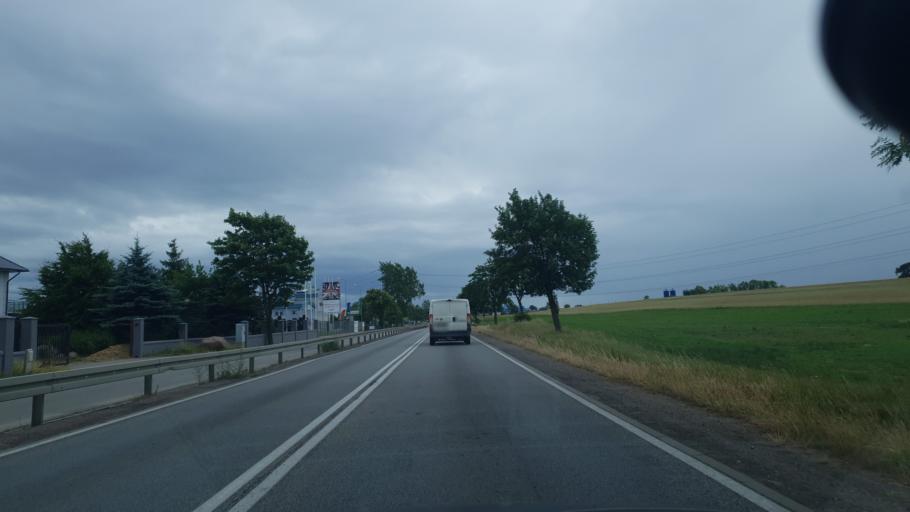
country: PL
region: Pomeranian Voivodeship
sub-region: Powiat kartuski
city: Zukowo
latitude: 54.3844
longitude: 18.3611
